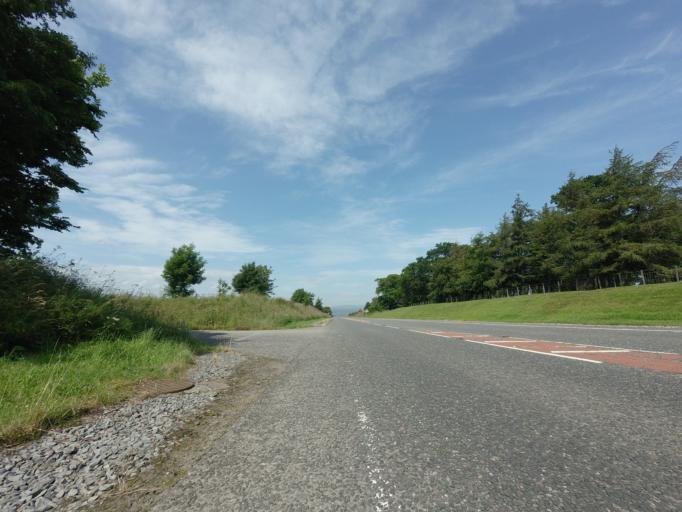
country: GB
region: Scotland
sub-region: Highland
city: Tain
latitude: 57.8243
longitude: -4.0785
